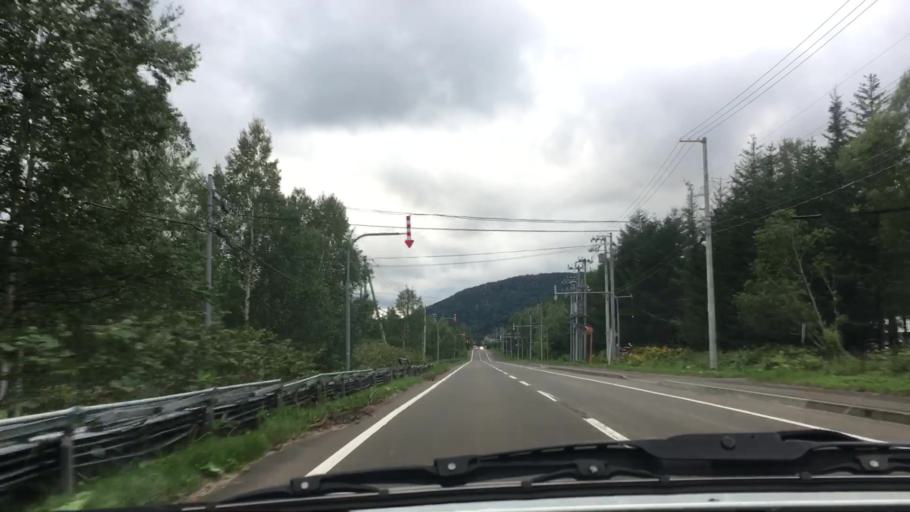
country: JP
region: Hokkaido
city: Shimo-furano
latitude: 43.0551
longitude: 142.6304
